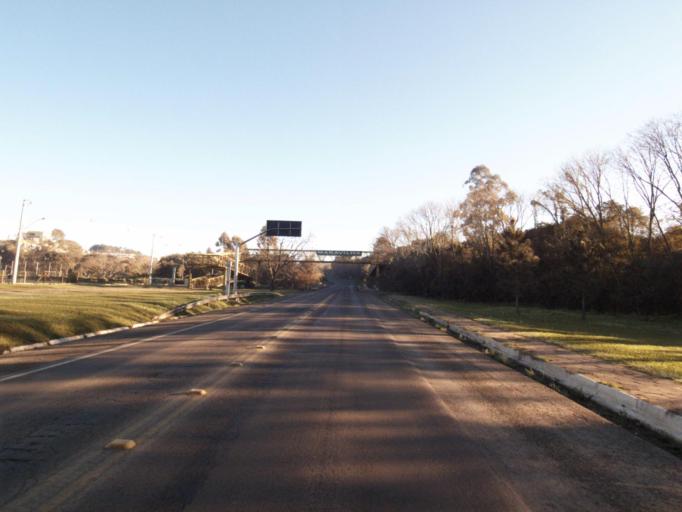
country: BR
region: Santa Catarina
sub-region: Sao Lourenco Do Oeste
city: Sao Lourenco dOeste
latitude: -26.7807
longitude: -53.1977
